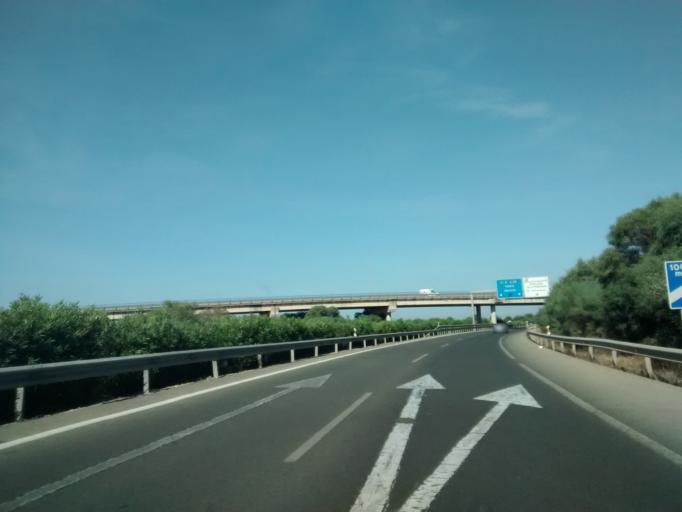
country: ES
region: Andalusia
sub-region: Provincia de Cadiz
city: Chiclana de la Frontera
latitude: 36.4444
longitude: -6.1433
